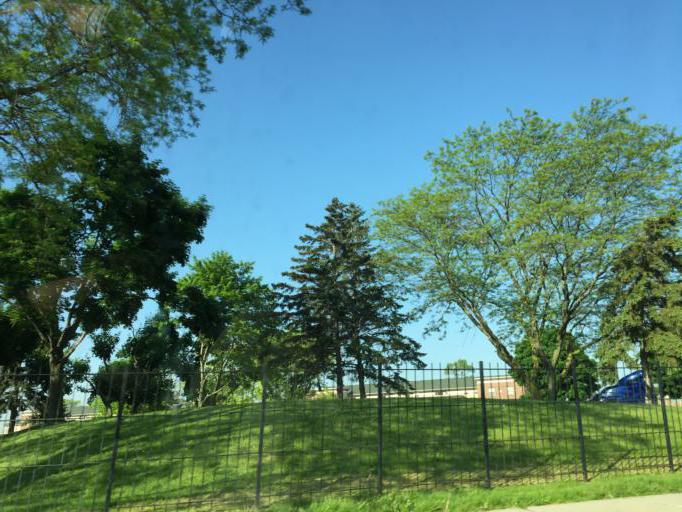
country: US
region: Michigan
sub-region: Wayne County
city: Detroit
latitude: 42.3441
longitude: -83.0780
